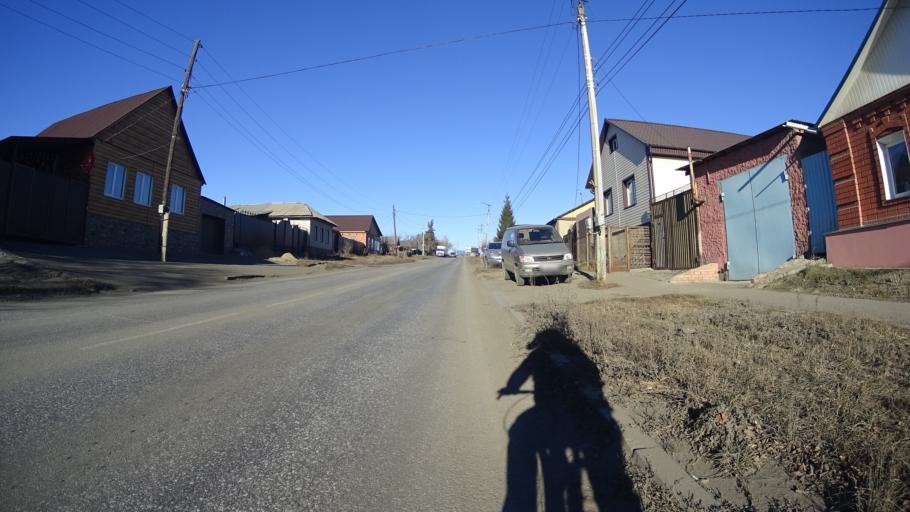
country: RU
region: Chelyabinsk
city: Troitsk
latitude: 54.1016
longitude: 61.5624
